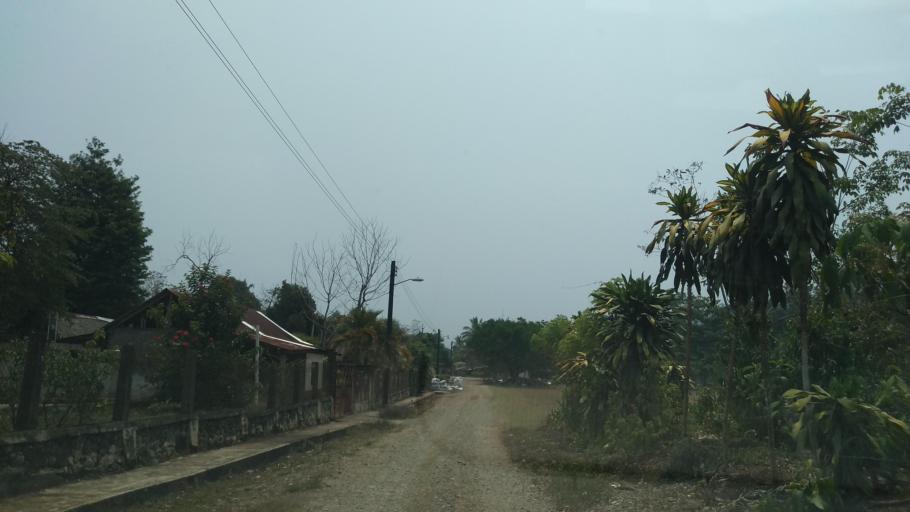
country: MX
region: Puebla
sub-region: San Sebastian Tlacotepec
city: San Martin Mazateopan
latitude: 18.4922
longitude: -96.7821
